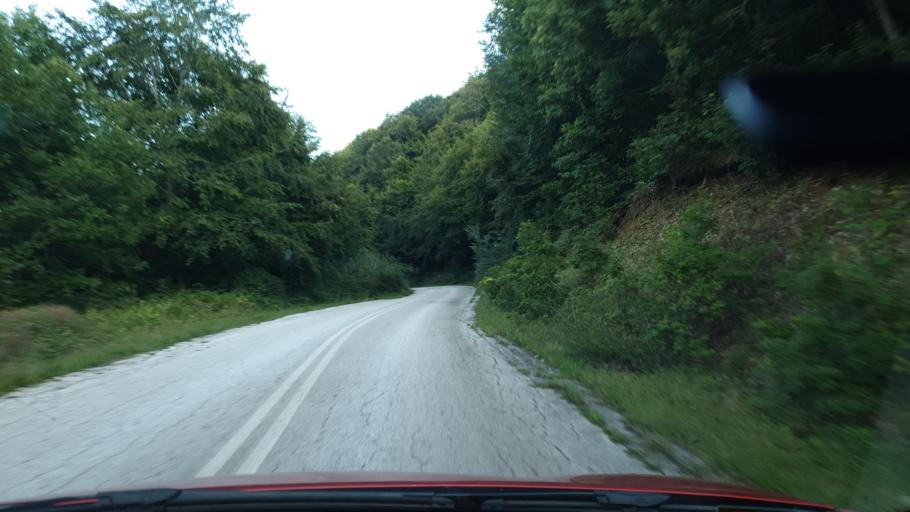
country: GR
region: Central Macedonia
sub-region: Nomos Chalkidikis
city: Galatista
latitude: 40.5104
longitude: 23.2532
